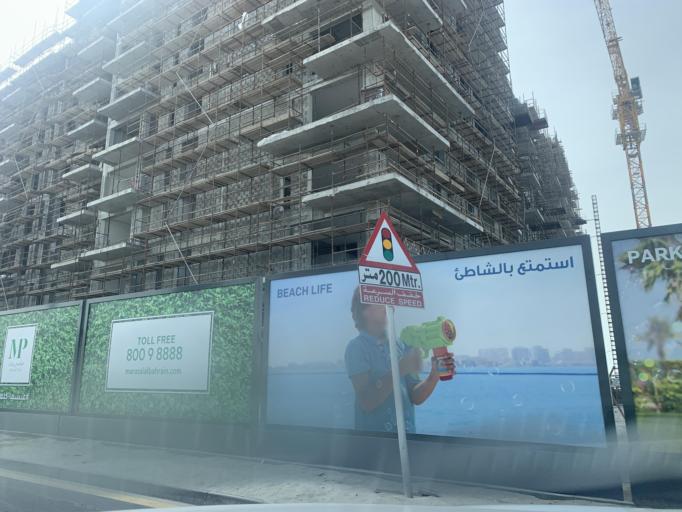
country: BH
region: Muharraq
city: Al Muharraq
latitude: 26.3074
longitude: 50.6461
